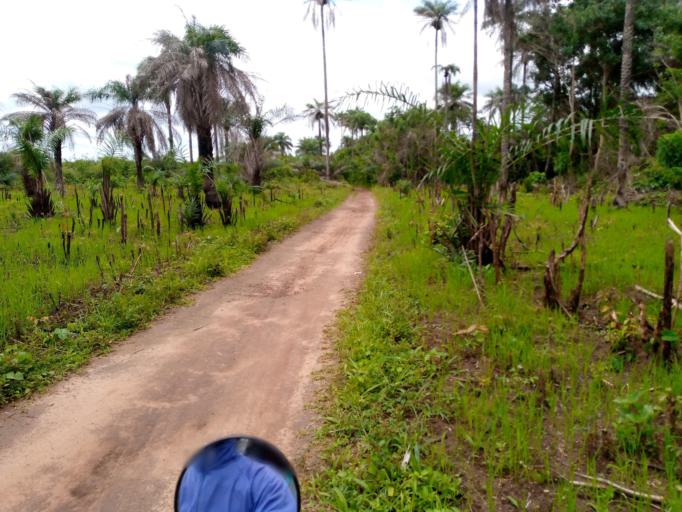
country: SL
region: Northern Province
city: Mange
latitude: 8.9916
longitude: -12.7767
